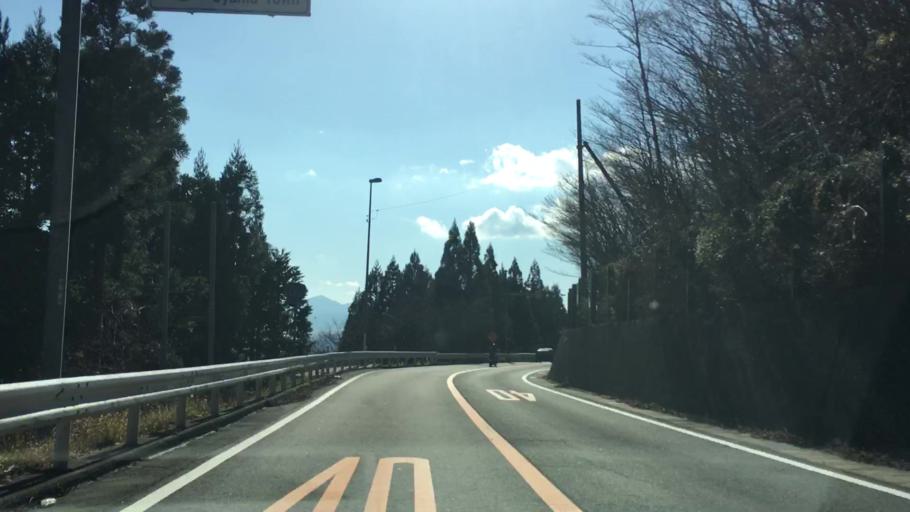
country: JP
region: Shizuoka
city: Gotemba
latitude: 35.3901
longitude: 138.8628
